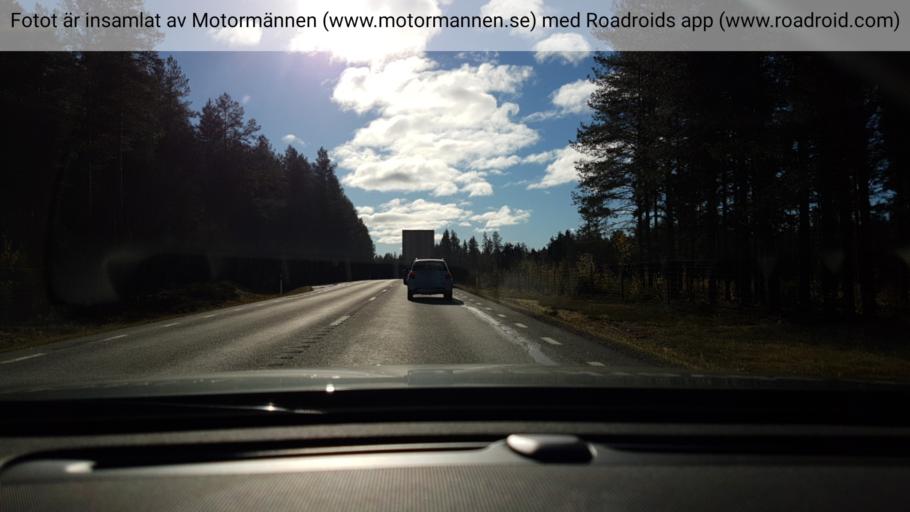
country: SE
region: Vaesterbotten
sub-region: Skelleftea Kommun
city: Burea
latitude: 64.4932
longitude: 21.2697
